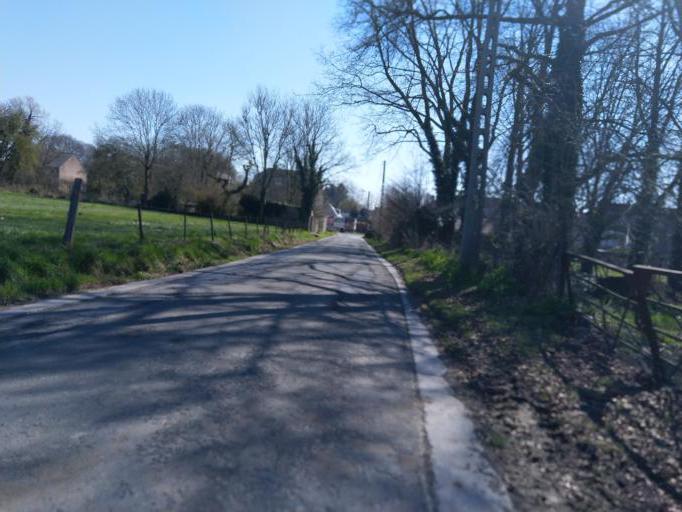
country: BE
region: Wallonia
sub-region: Province du Hainaut
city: Soignies
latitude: 50.5166
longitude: 4.0119
